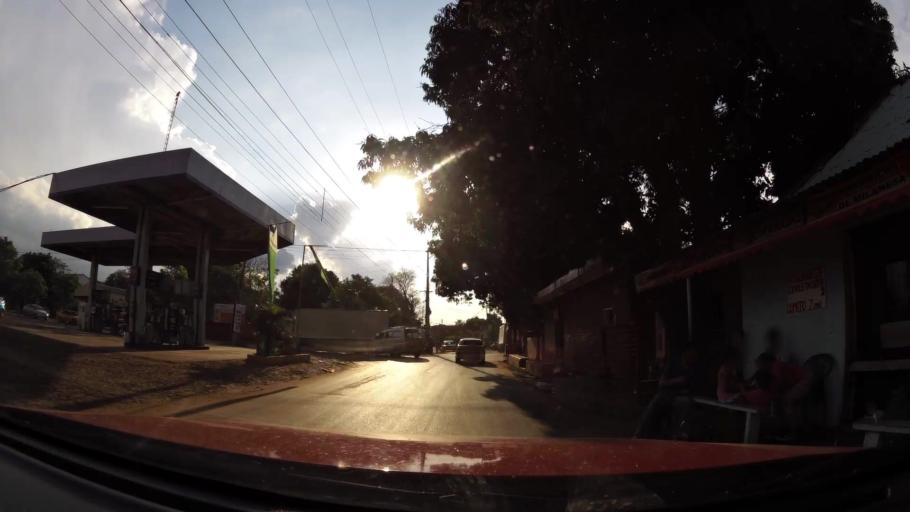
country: PY
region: Central
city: Fernando de la Mora
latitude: -25.3505
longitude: -57.5218
